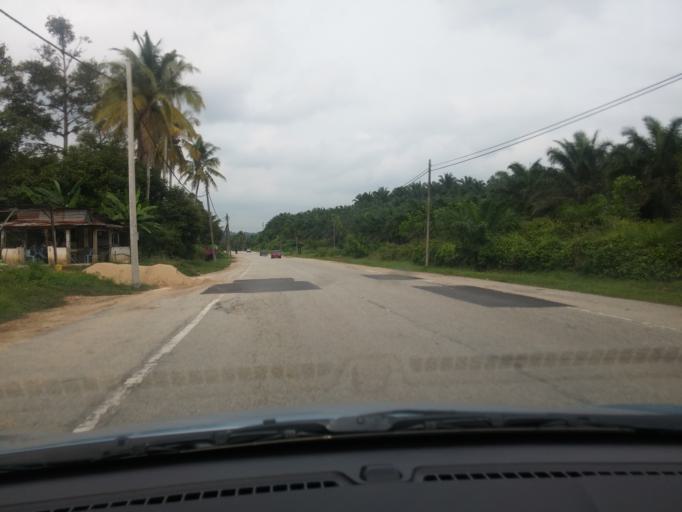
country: MY
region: Pahang
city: Kuantan
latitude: 3.8826
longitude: 103.1675
